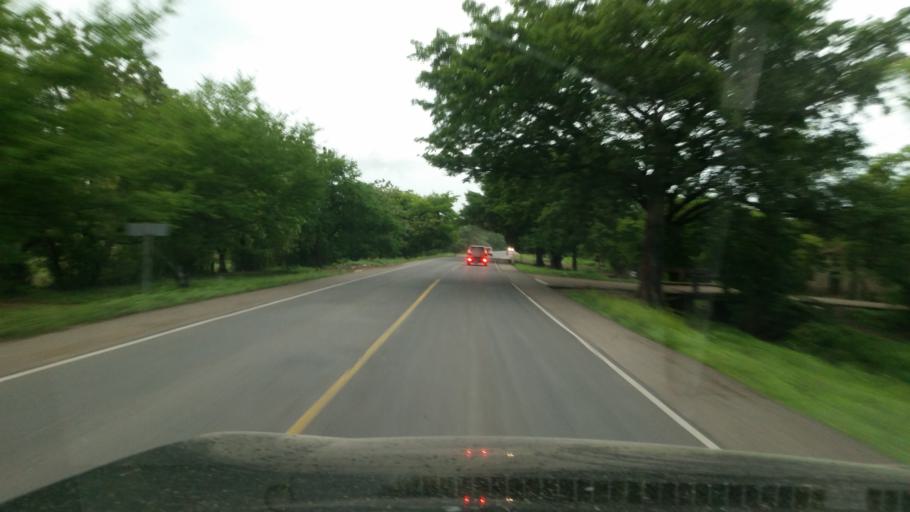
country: NI
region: Chinandega
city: Puerto Morazan
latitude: 12.7750
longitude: -87.0539
